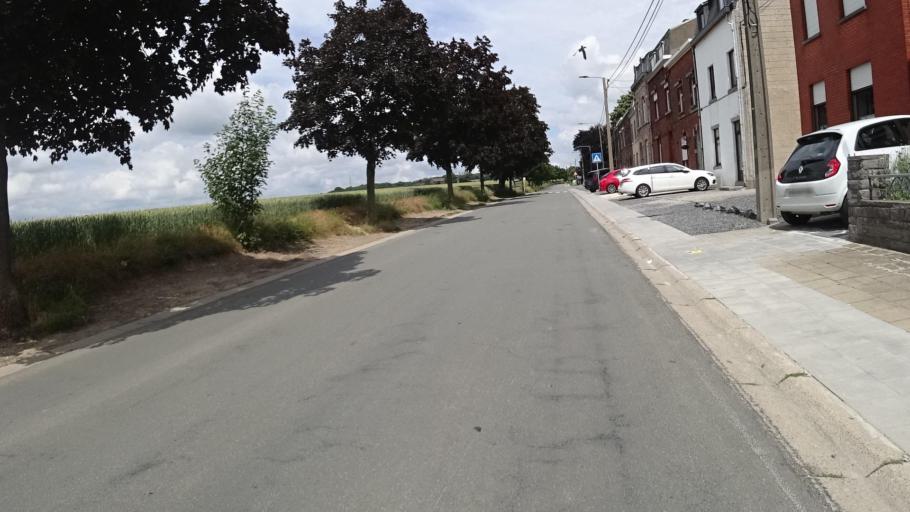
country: BE
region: Wallonia
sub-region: Province de Namur
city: Namur
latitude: 50.4780
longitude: 4.8628
